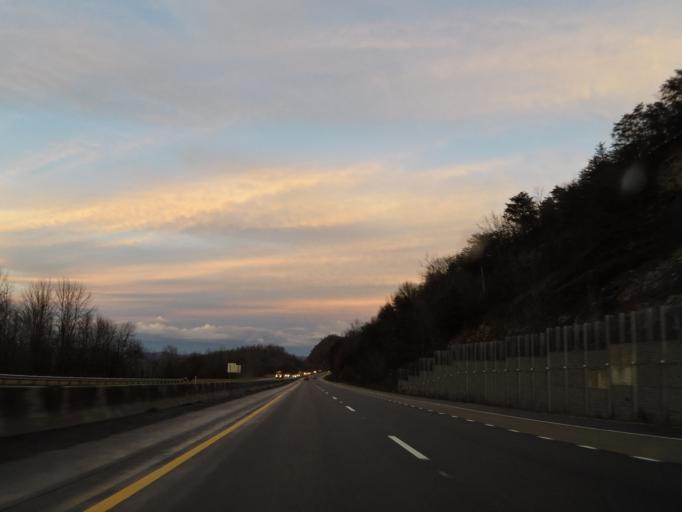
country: US
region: Tennessee
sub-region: Campbell County
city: Jellico
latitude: 36.5404
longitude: -84.1590
